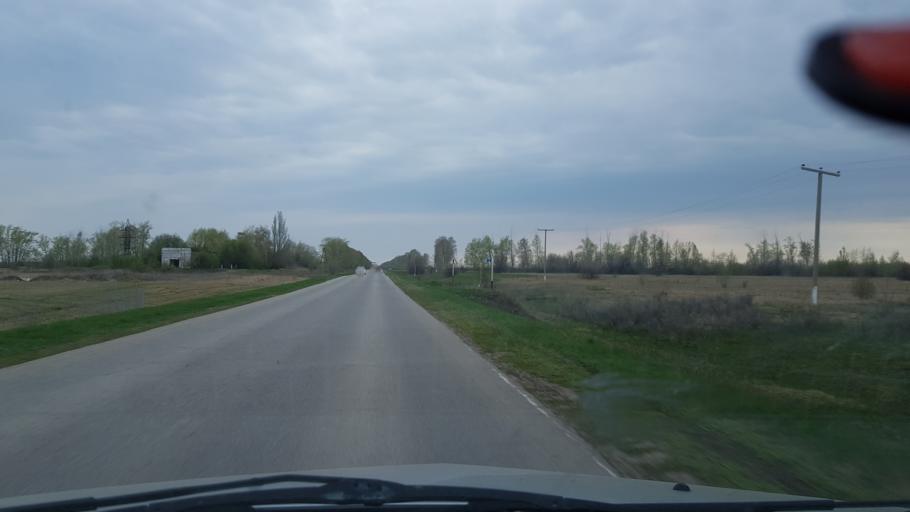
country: RU
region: Samara
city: Tol'yatti
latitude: 53.6577
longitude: 49.2460
